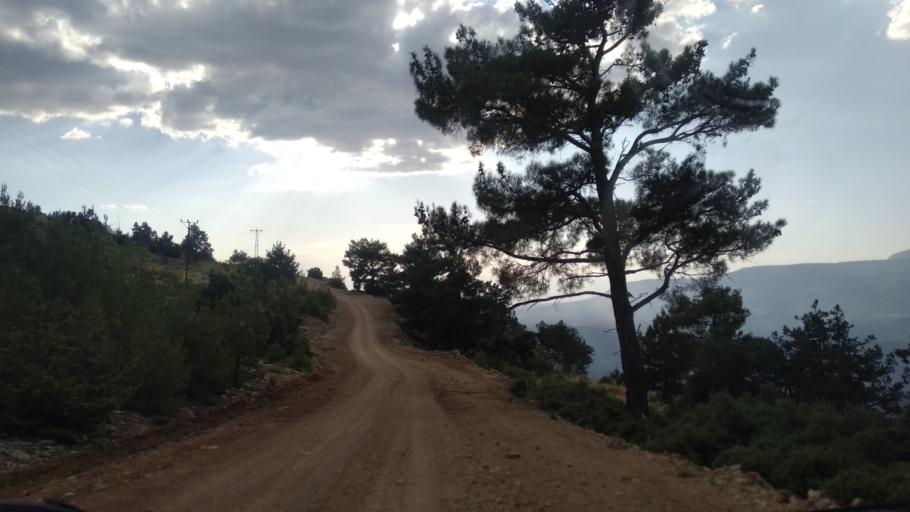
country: TR
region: Mersin
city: Sarikavak
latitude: 36.5980
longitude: 33.6915
